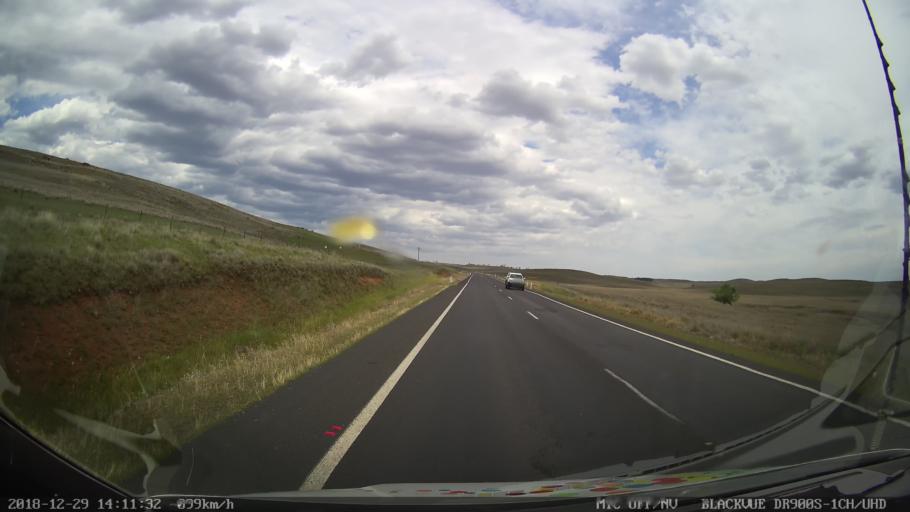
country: AU
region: New South Wales
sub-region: Cooma-Monaro
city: Cooma
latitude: -36.4071
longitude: 149.2212
